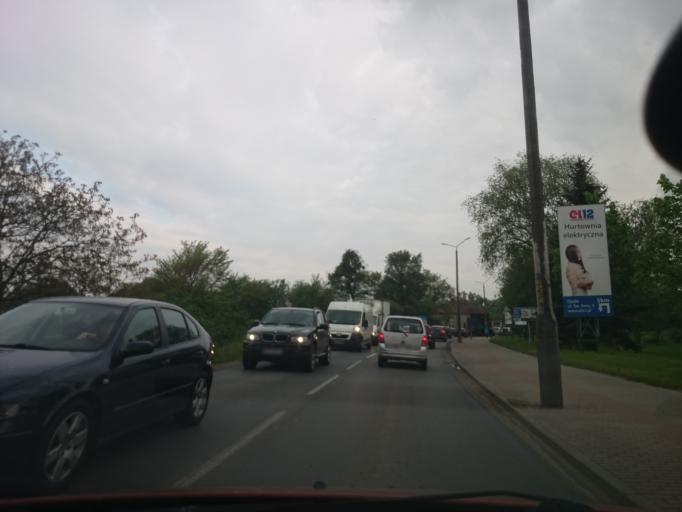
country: PL
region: Opole Voivodeship
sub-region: Powiat opolski
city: Czarnowasy
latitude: 50.7211
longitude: 17.9014
